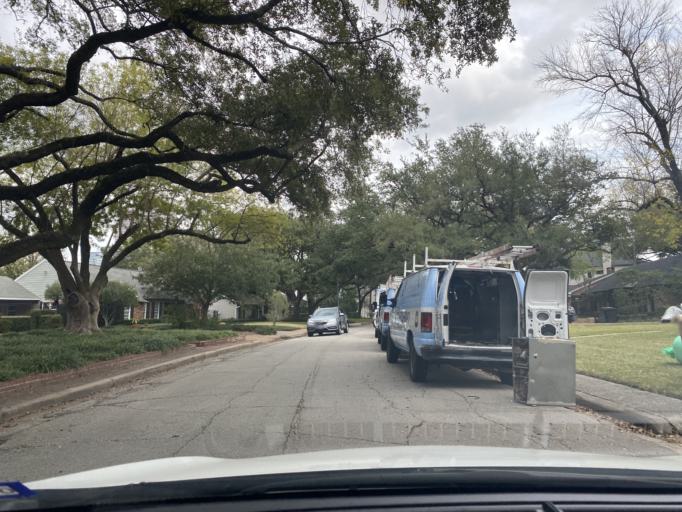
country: US
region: Texas
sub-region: Harris County
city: Hunters Creek Village
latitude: 29.7480
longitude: -95.4699
